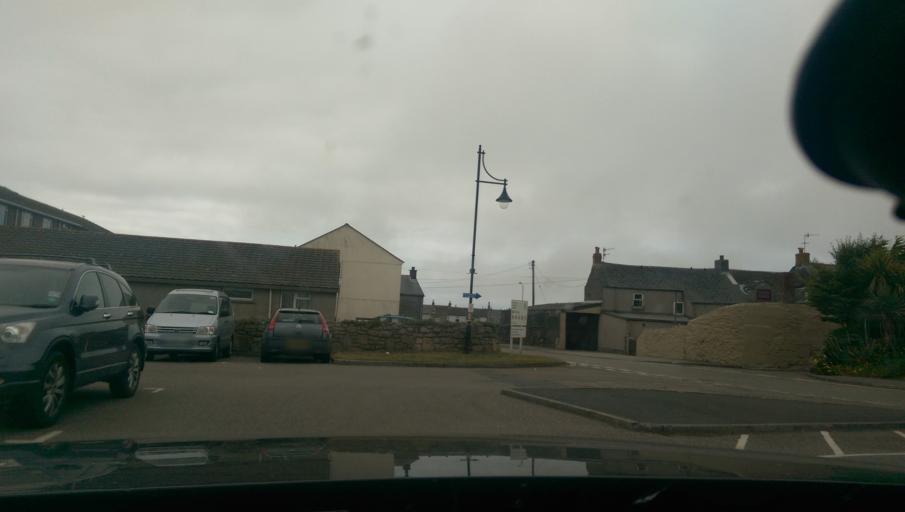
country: GB
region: England
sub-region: Cornwall
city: Saint Just
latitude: 50.1237
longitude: -5.6818
